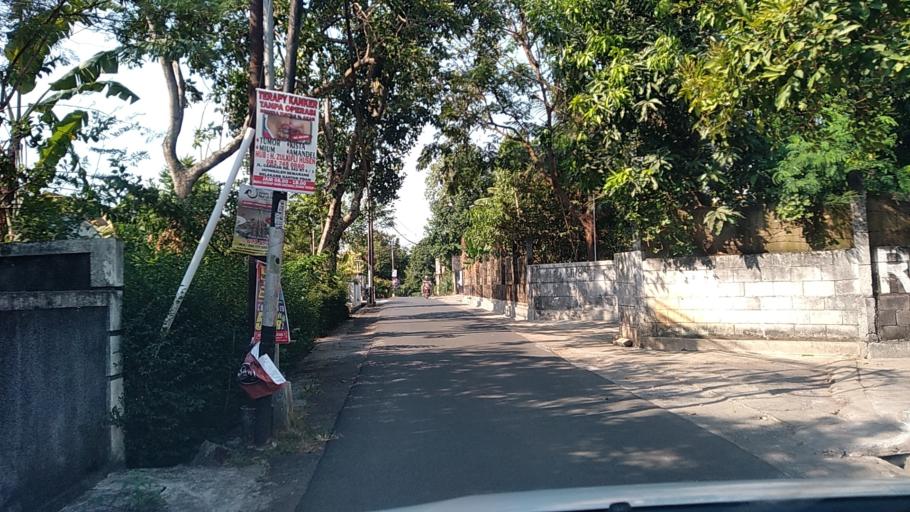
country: ID
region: Central Java
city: Semarang
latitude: -7.0613
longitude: 110.4211
